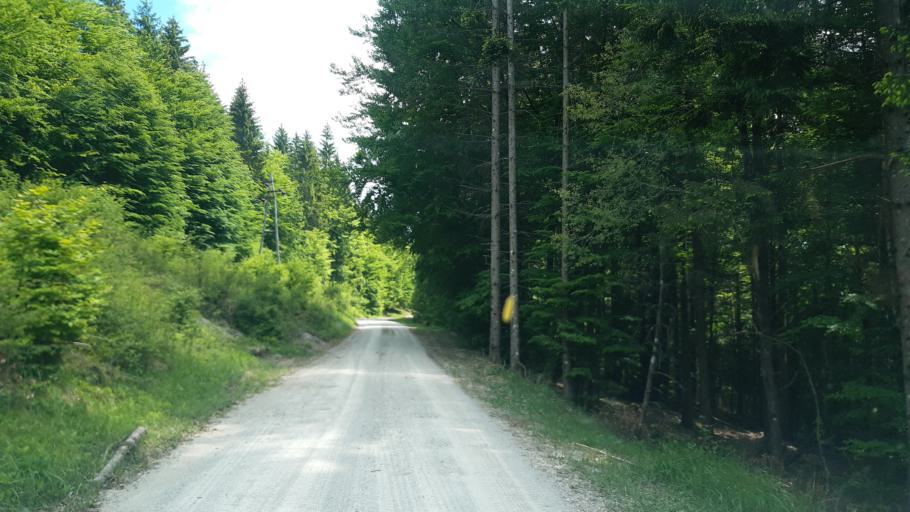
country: SI
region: Kocevje
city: Kocevje
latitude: 45.6297
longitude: 15.0010
